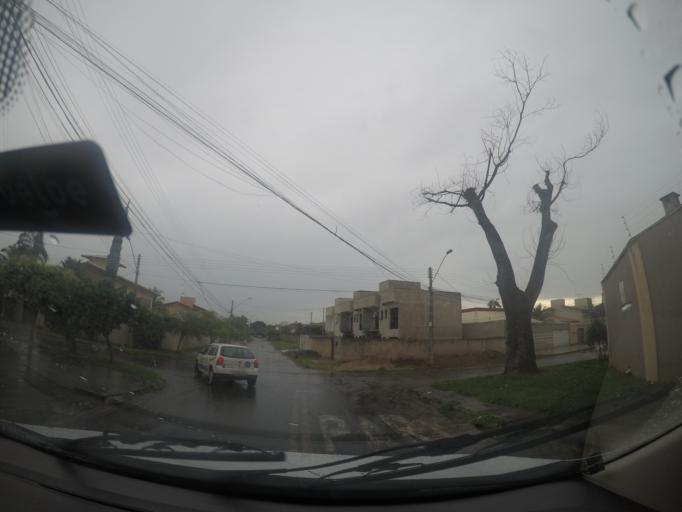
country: BR
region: Goias
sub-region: Goiania
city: Goiania
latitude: -16.6469
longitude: -49.2317
